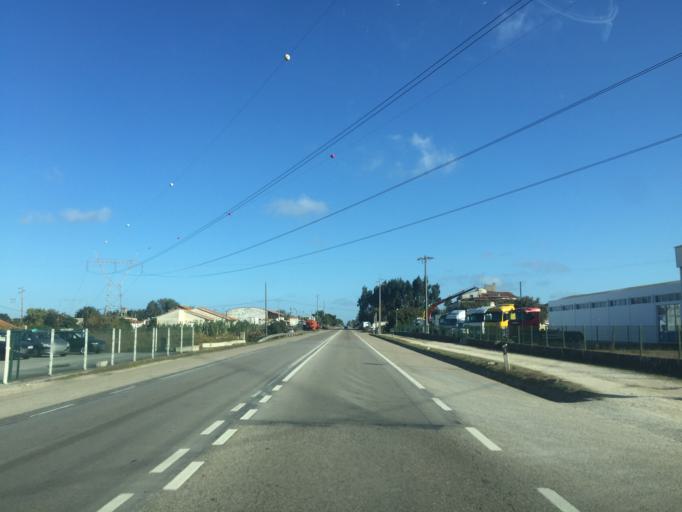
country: PT
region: Leiria
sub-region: Alcobaca
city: Benedita
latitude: 39.4373
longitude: -8.9553
